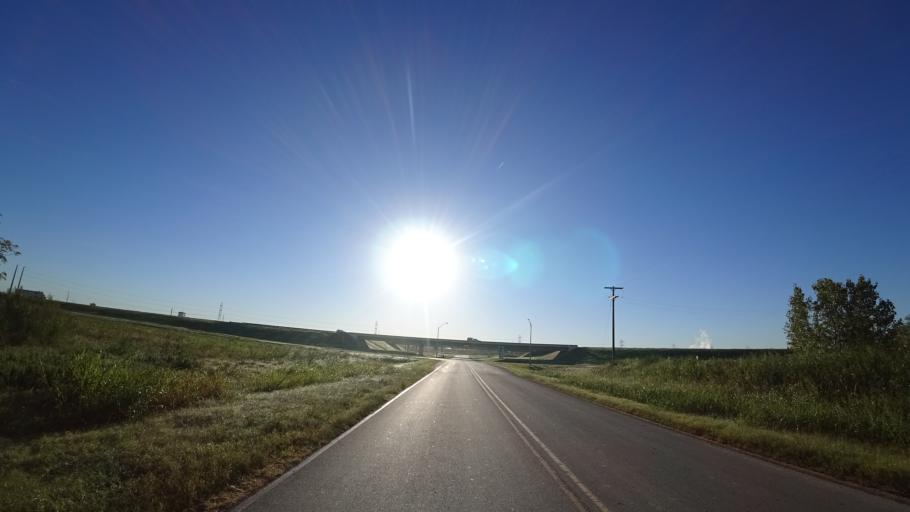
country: US
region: Texas
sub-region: Travis County
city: Hornsby Bend
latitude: 30.2298
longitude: -97.6217
